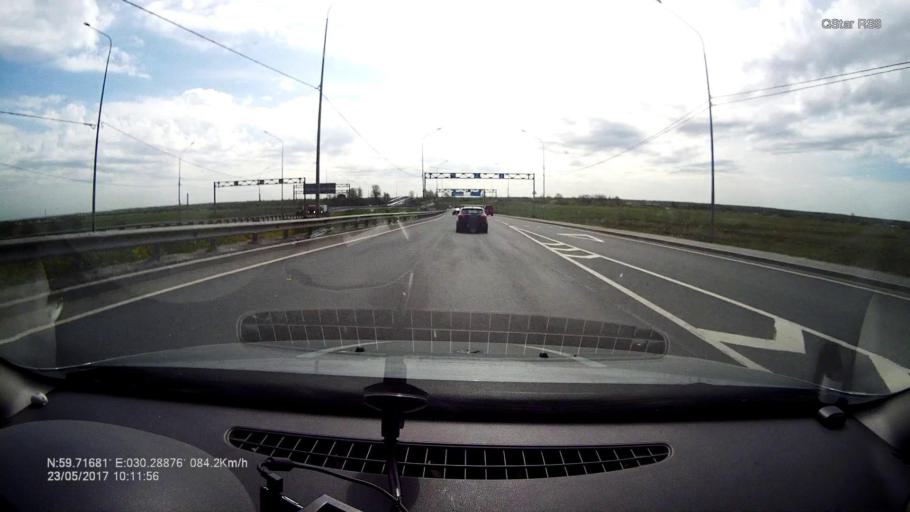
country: RU
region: St.-Petersburg
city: Aleksandrovskaya
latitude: 59.7167
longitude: 30.2892
